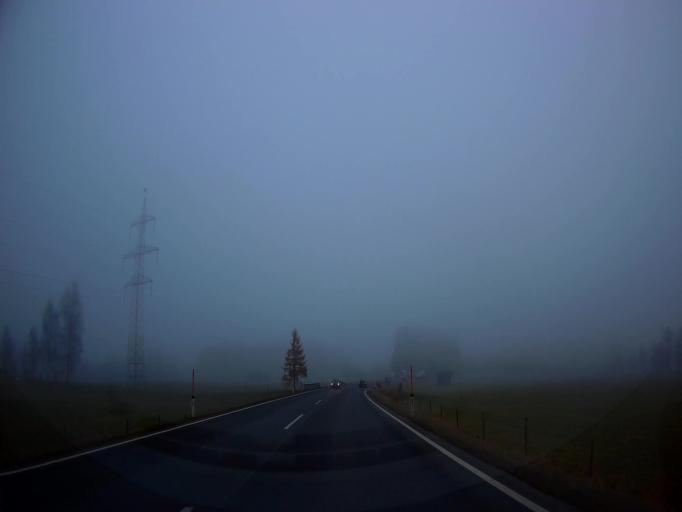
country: AT
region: Salzburg
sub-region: Politischer Bezirk Zell am See
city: Maishofen
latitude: 47.3850
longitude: 12.8068
